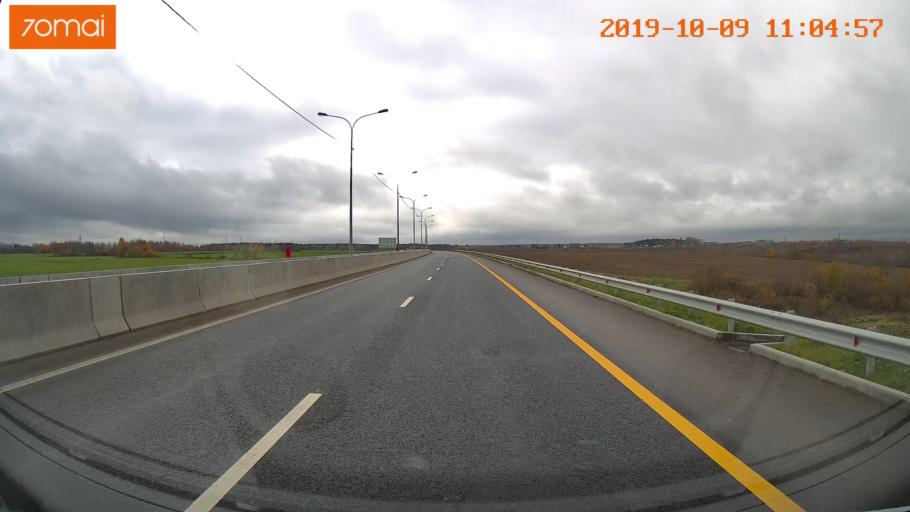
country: RU
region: Vologda
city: Molochnoye
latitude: 59.2059
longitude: 39.7615
